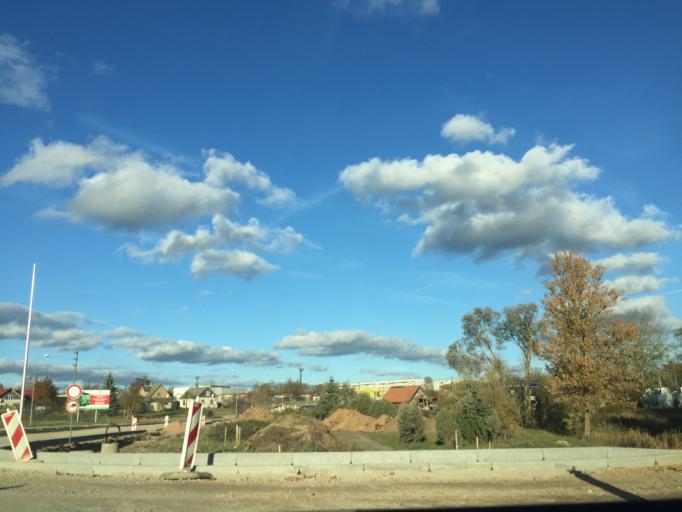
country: LV
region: Tukuma Rajons
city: Tukums
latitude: 56.9704
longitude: 23.1372
